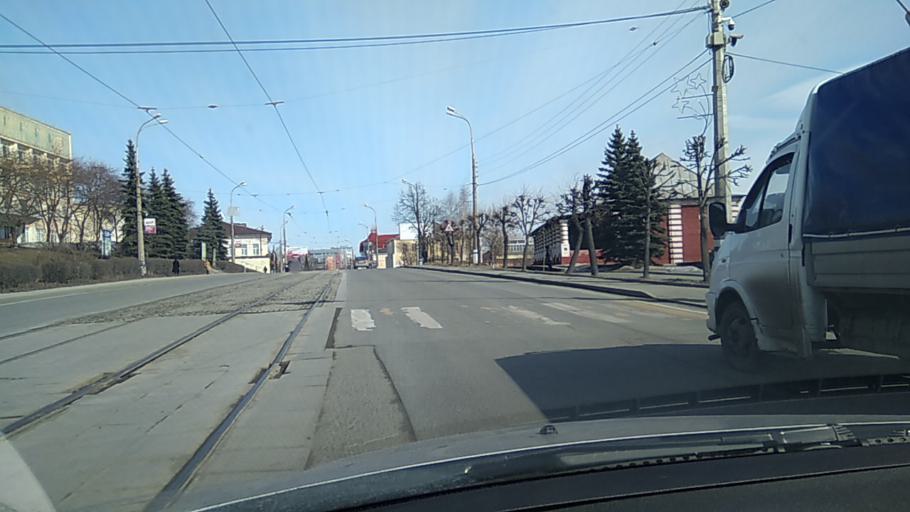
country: RU
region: Sverdlovsk
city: Nizhniy Tagil
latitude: 57.9059
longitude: 59.9515
